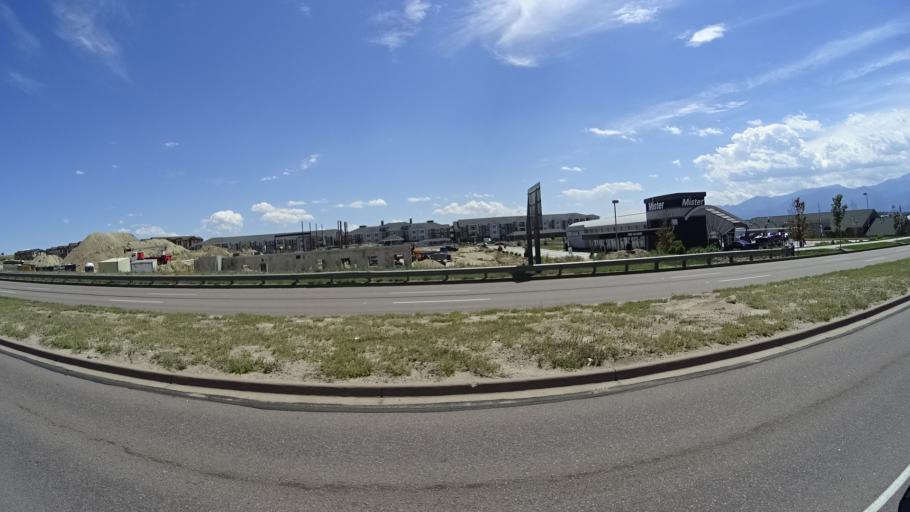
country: US
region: Colorado
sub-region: El Paso County
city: Black Forest
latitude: 38.9403
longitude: -104.7266
